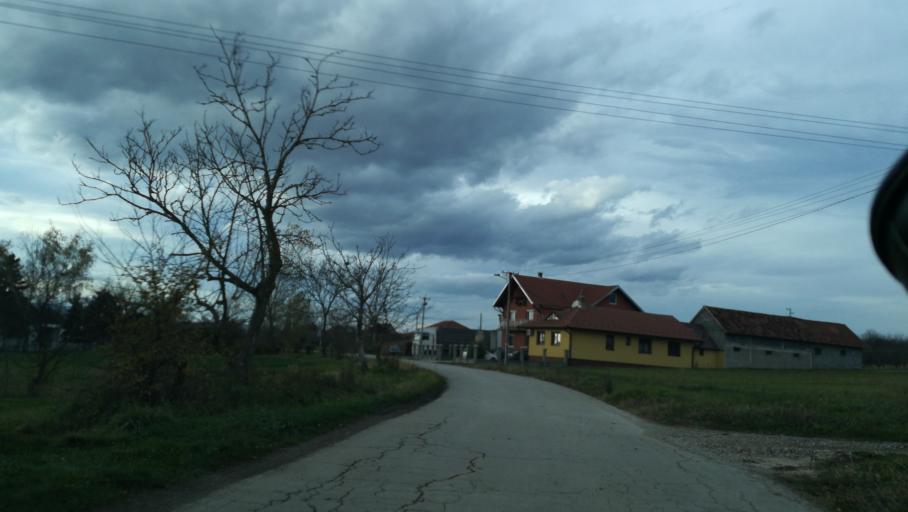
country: RS
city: Prislonica
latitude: 43.9136
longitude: 20.4229
